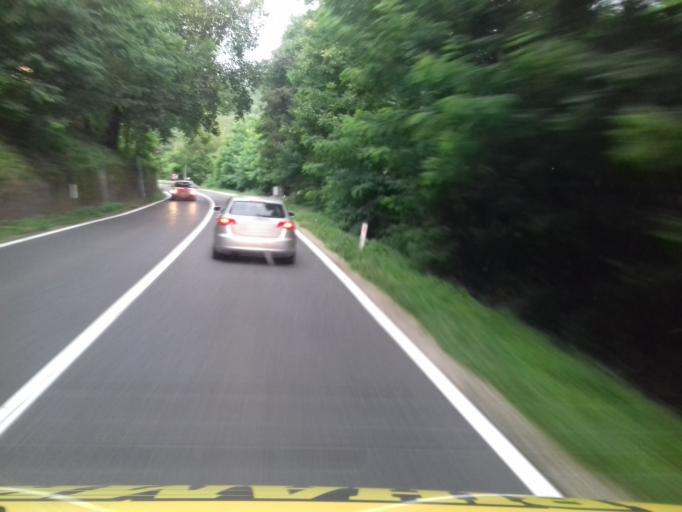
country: BA
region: Federation of Bosnia and Herzegovina
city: Konjic
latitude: 43.6866
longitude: 17.8759
